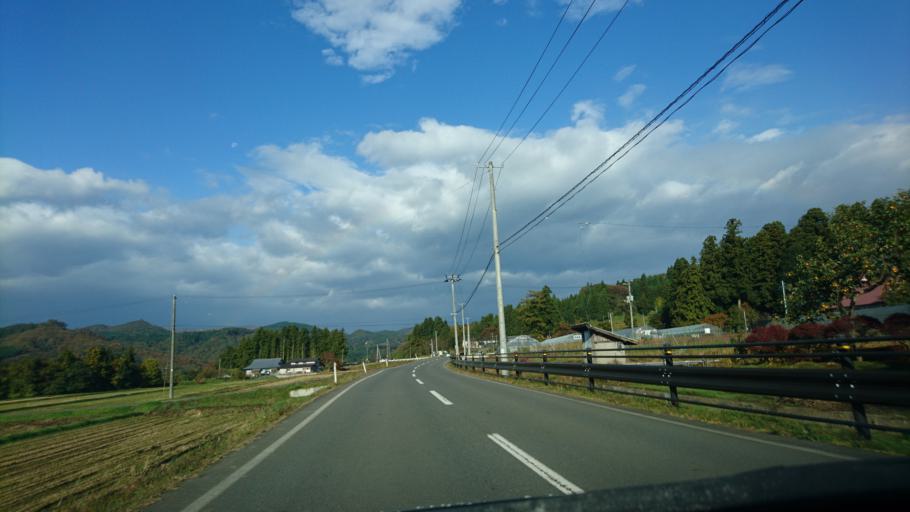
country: JP
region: Iwate
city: Mizusawa
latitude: 39.0454
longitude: 141.0574
